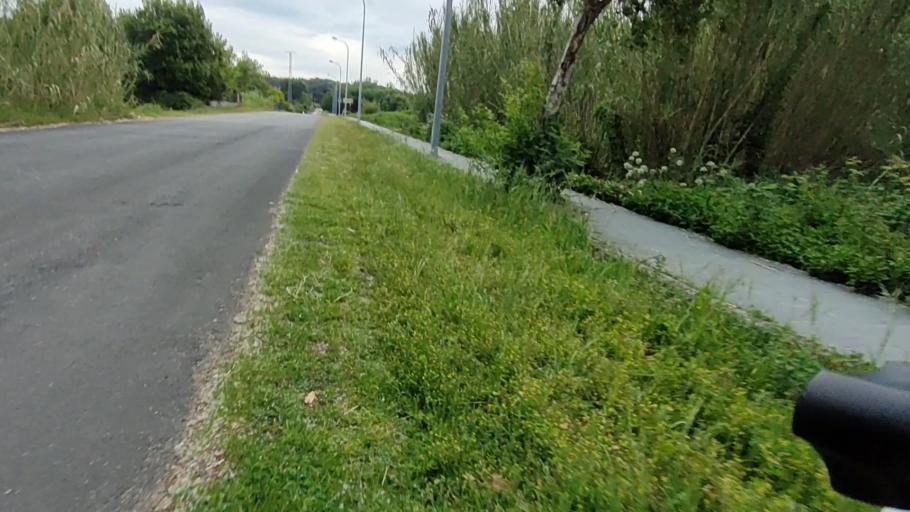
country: ES
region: Galicia
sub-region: Provincia da Coruna
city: Boiro
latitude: 42.6122
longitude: -8.8676
